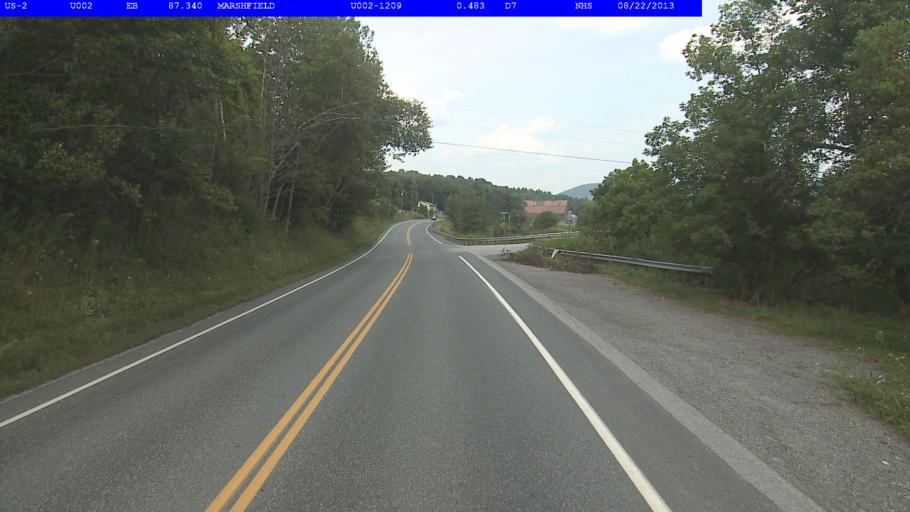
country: US
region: Vermont
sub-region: Washington County
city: Barre
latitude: 44.2843
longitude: -72.4150
